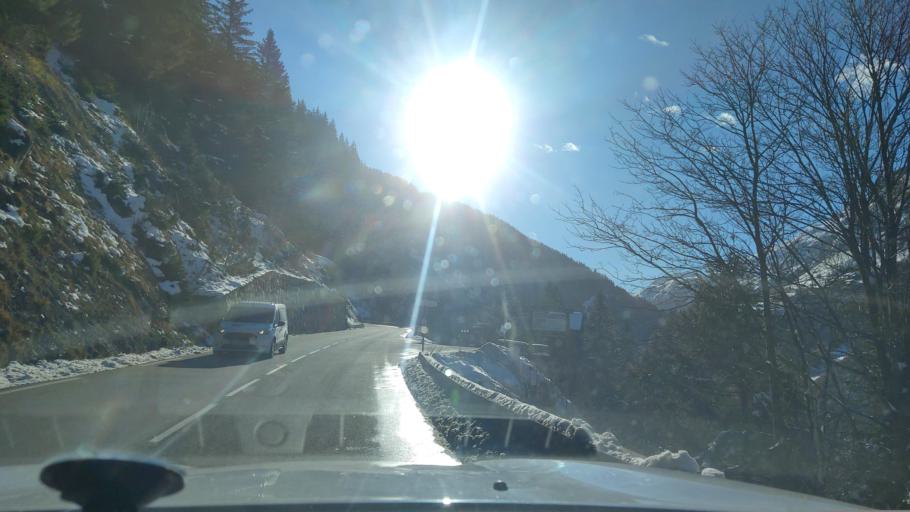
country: FR
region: Rhone-Alpes
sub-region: Departement de la Savoie
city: Tignes
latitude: 45.5436
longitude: 6.9090
